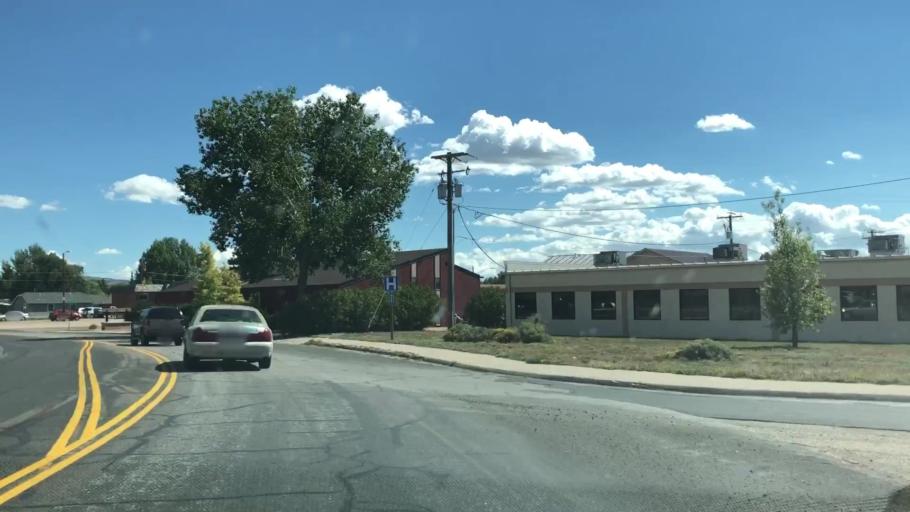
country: US
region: Wyoming
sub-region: Albany County
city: Laramie
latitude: 41.3262
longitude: -105.5904
